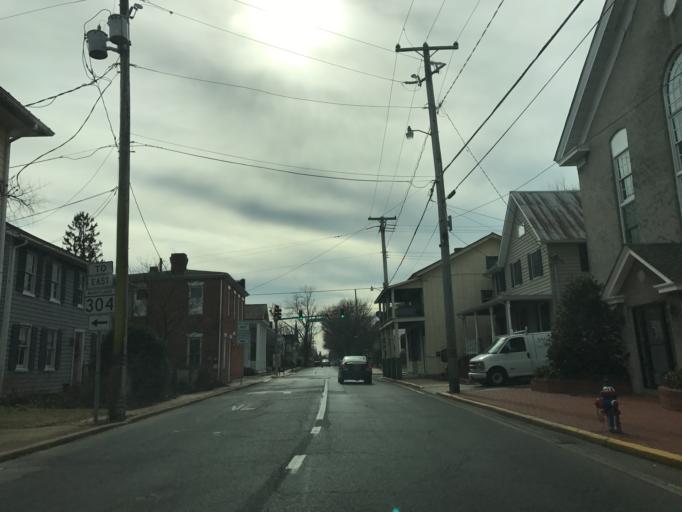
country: US
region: Maryland
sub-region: Queen Anne's County
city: Centreville
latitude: 39.0455
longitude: -76.0660
